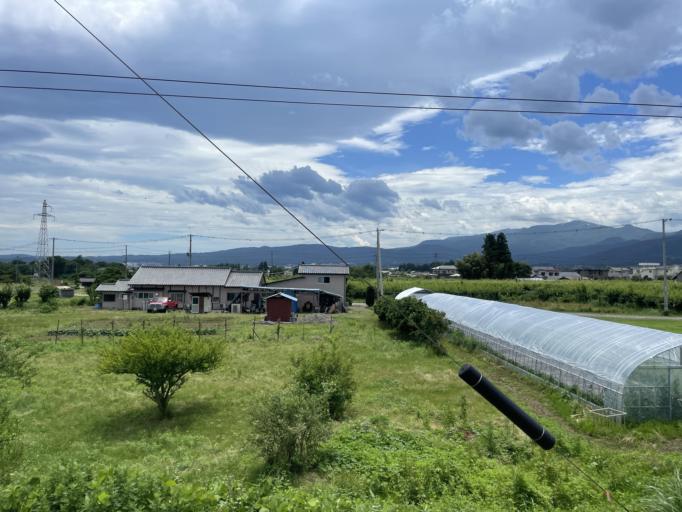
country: JP
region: Fukushima
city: Fukushima-shi
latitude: 37.7704
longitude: 140.3975
